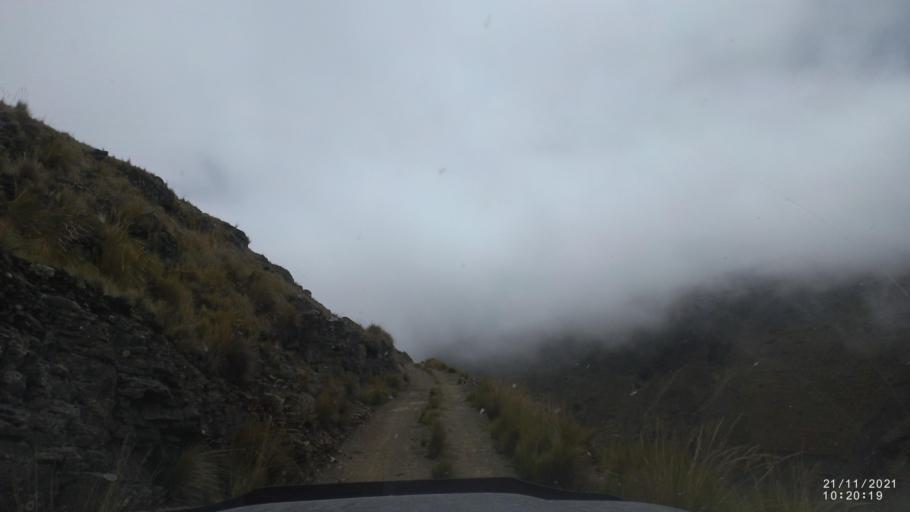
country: BO
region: Cochabamba
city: Cochabamba
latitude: -16.9915
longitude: -66.2618
